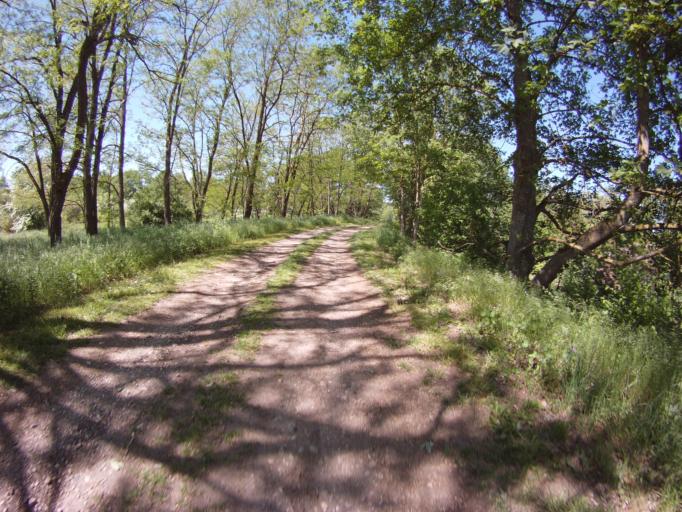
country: FR
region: Lorraine
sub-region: Departement de Meurthe-et-Moselle
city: Dommartin-les-Toul
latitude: 48.6548
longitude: 5.9008
